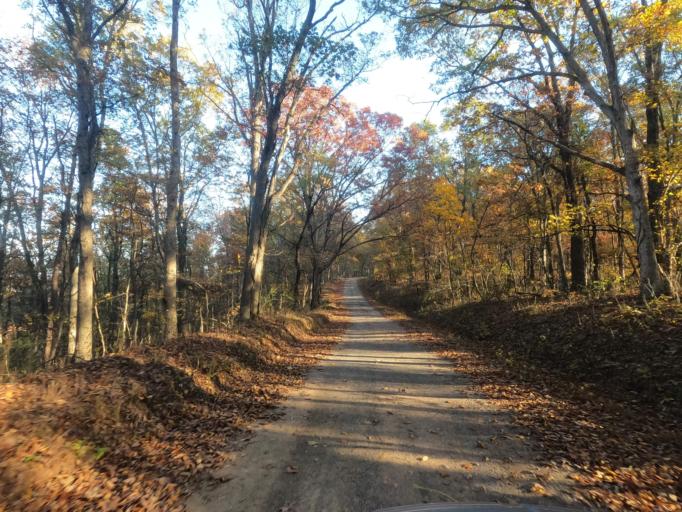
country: US
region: West Virginia
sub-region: Mineral County
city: Fort Ashby
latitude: 39.5371
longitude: -78.5355
